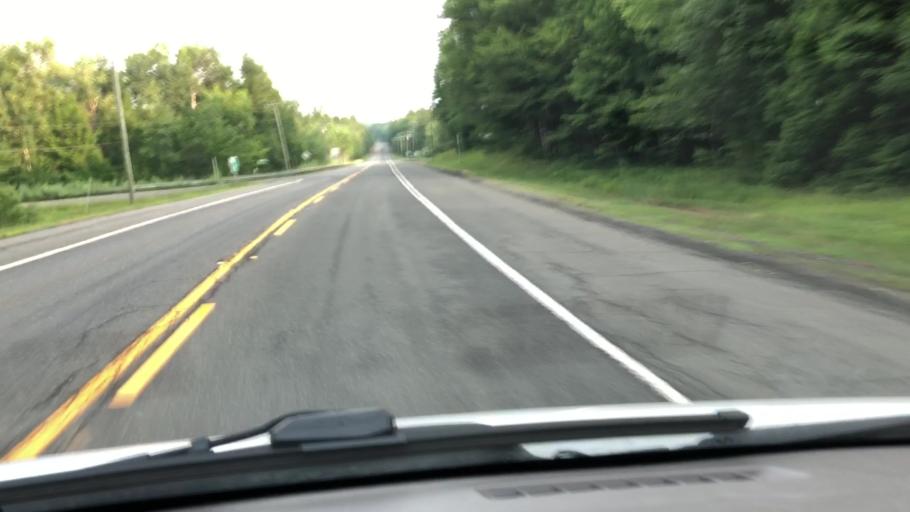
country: US
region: Massachusetts
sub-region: Berkshire County
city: Hinsdale
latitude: 42.4834
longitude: -72.9862
